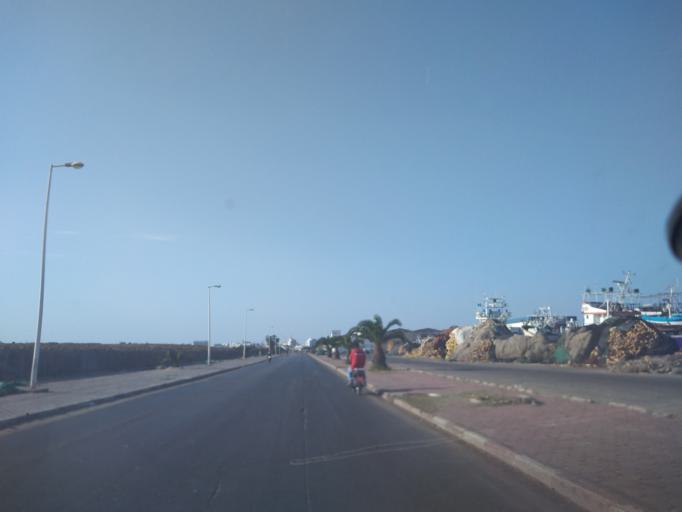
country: TN
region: Safaqis
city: Sfax
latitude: 34.7159
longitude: 10.7609
